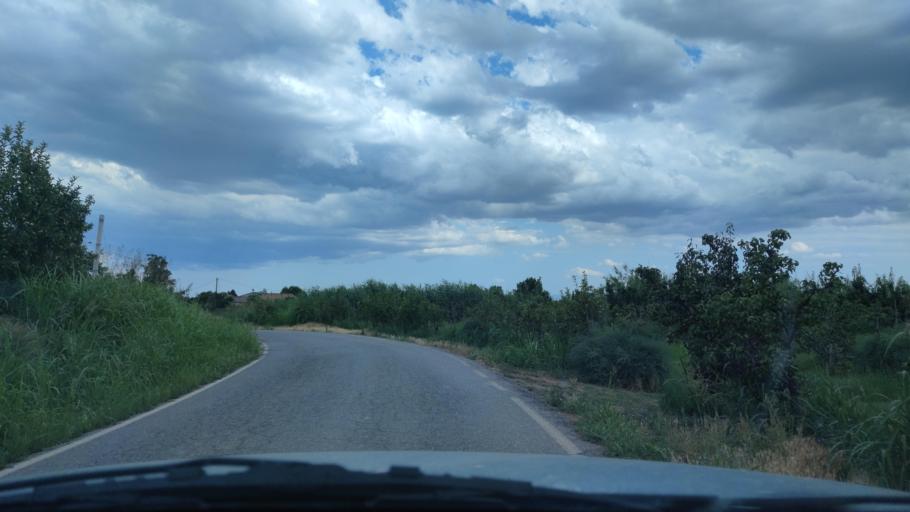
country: ES
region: Catalonia
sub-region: Provincia de Lleida
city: Lleida
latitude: 41.6239
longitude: 0.5794
